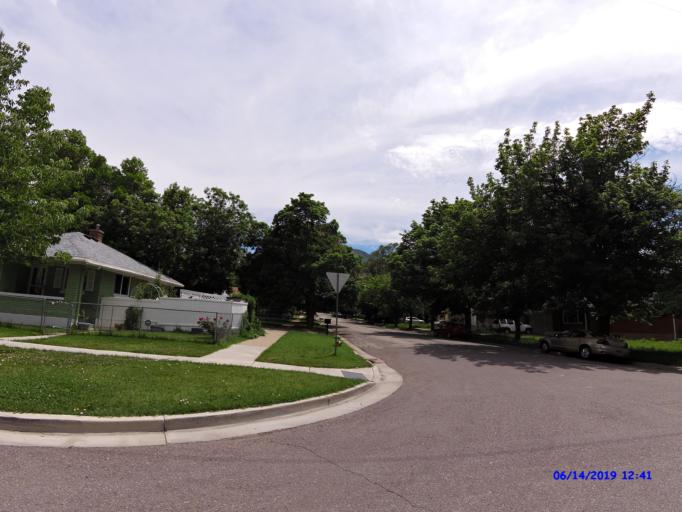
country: US
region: Utah
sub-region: Weber County
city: Ogden
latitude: 41.2278
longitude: -111.9536
